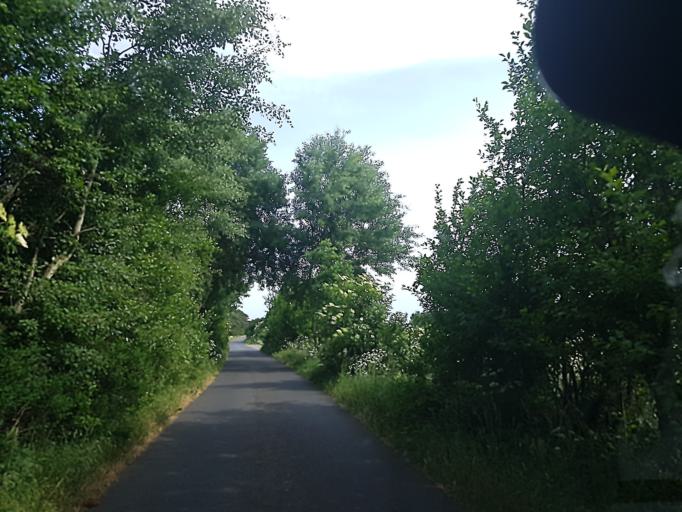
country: DE
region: Brandenburg
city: Niemegk
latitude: 52.0069
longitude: 12.6651
